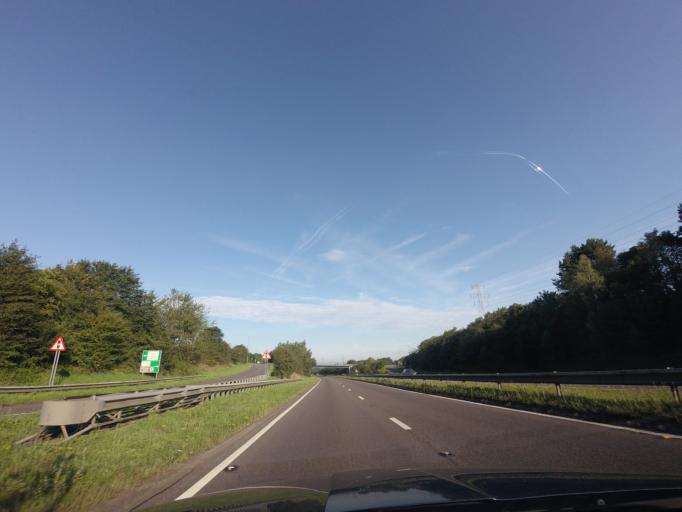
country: GB
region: England
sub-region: Derbyshire
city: Pilsley
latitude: 53.2075
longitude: -1.3759
